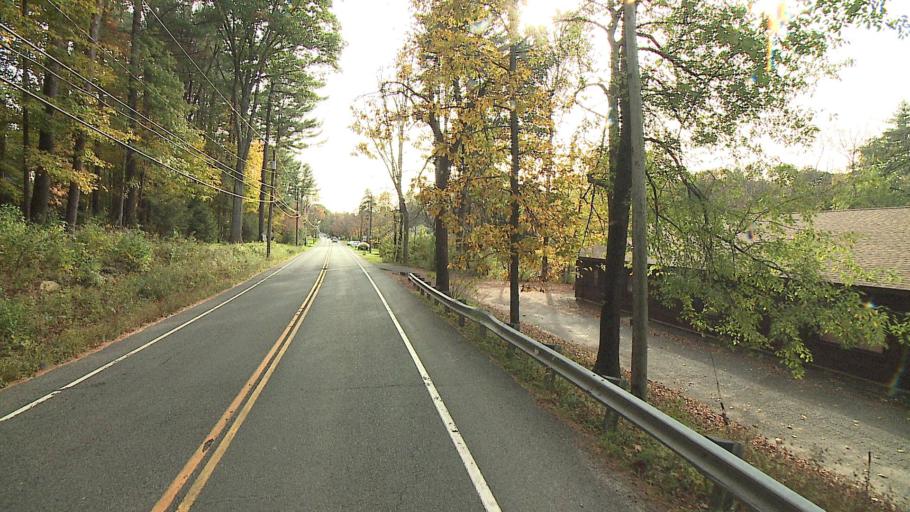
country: US
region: Connecticut
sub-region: Litchfield County
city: Canaan
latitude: 42.0148
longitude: -73.3523
